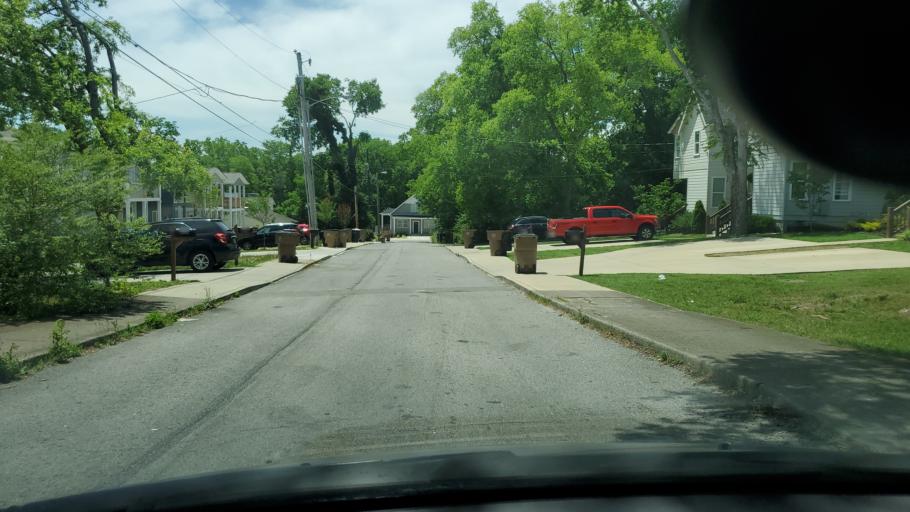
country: US
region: Tennessee
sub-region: Davidson County
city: Nashville
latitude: 36.2049
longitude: -86.7410
